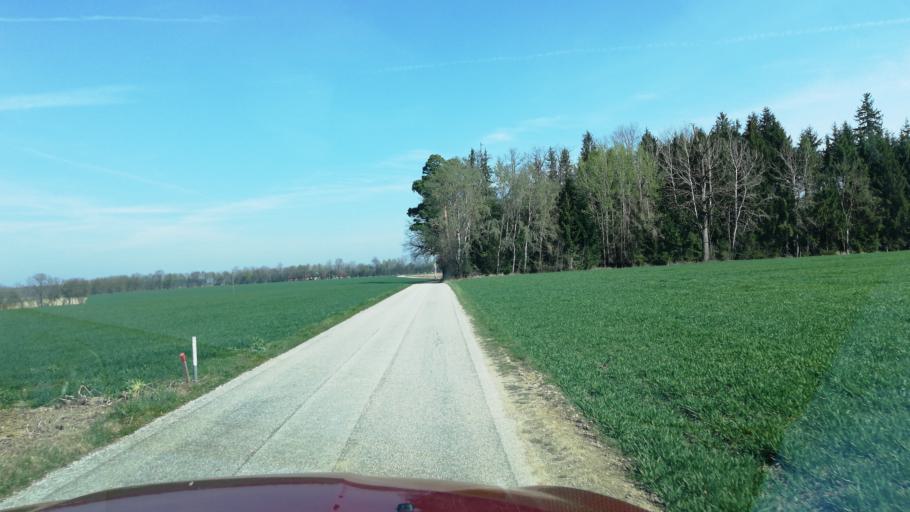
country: AT
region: Upper Austria
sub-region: Wels-Land
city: Sattledt
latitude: 48.1124
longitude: 14.0719
